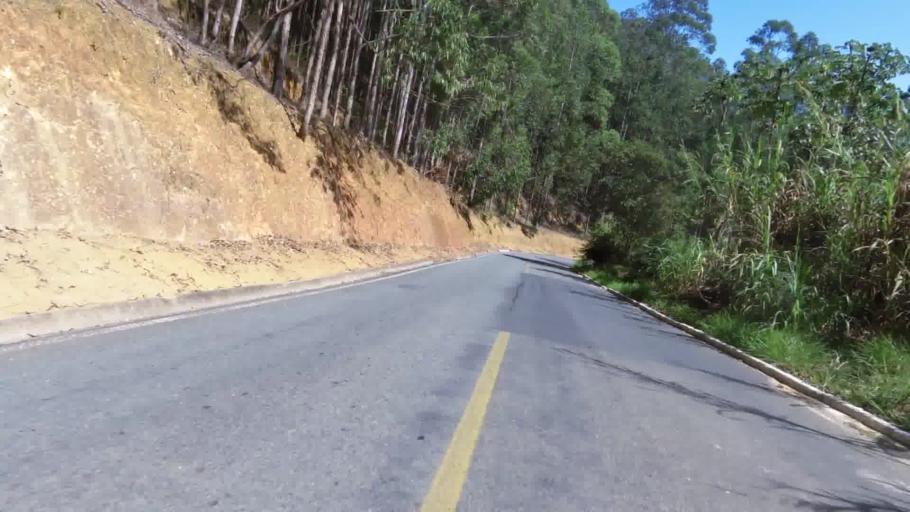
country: BR
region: Espirito Santo
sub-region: Marechal Floriano
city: Marechal Floriano
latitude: -20.4230
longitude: -40.8757
